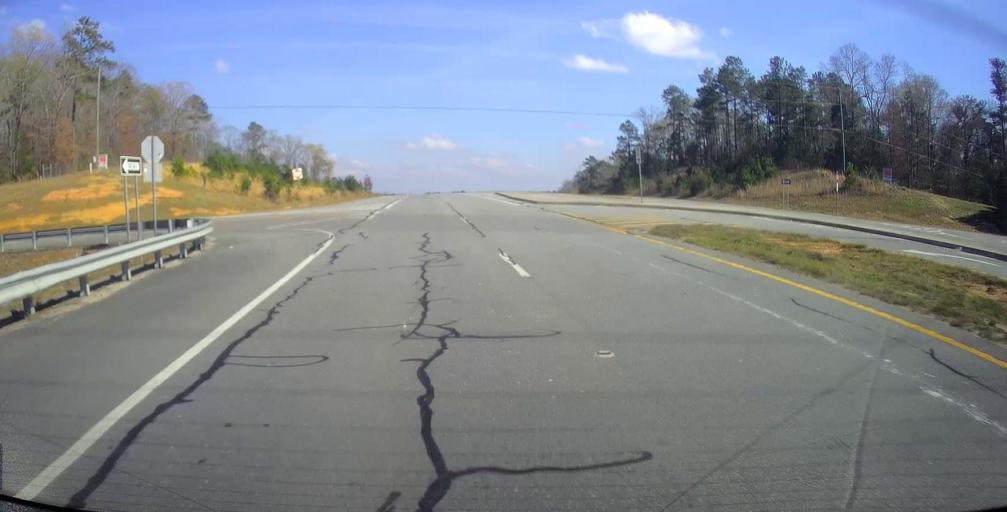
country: US
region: Georgia
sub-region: Wilkinson County
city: Gordon
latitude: 32.9004
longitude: -83.3414
